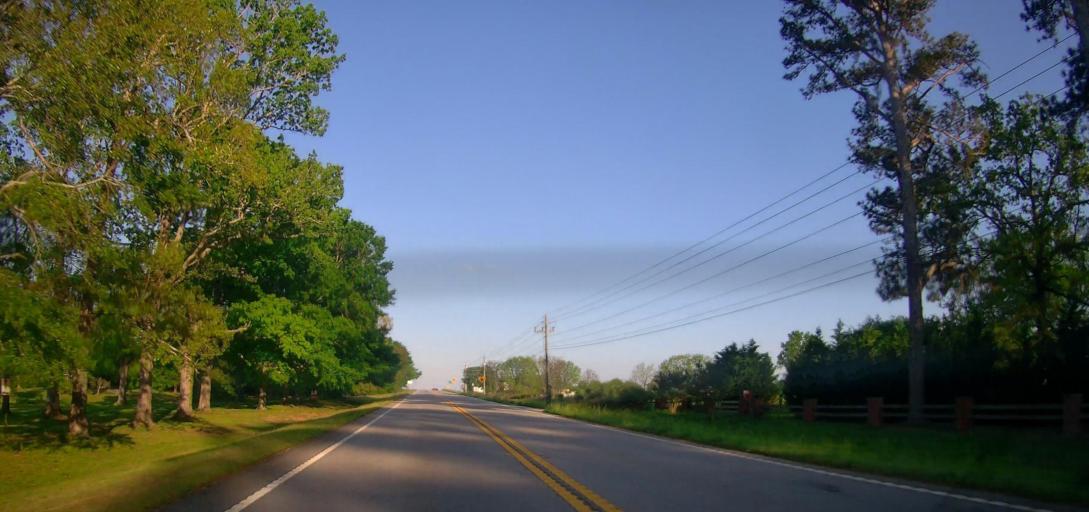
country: US
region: Georgia
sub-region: Walton County
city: Social Circle
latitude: 33.5540
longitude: -83.7419
